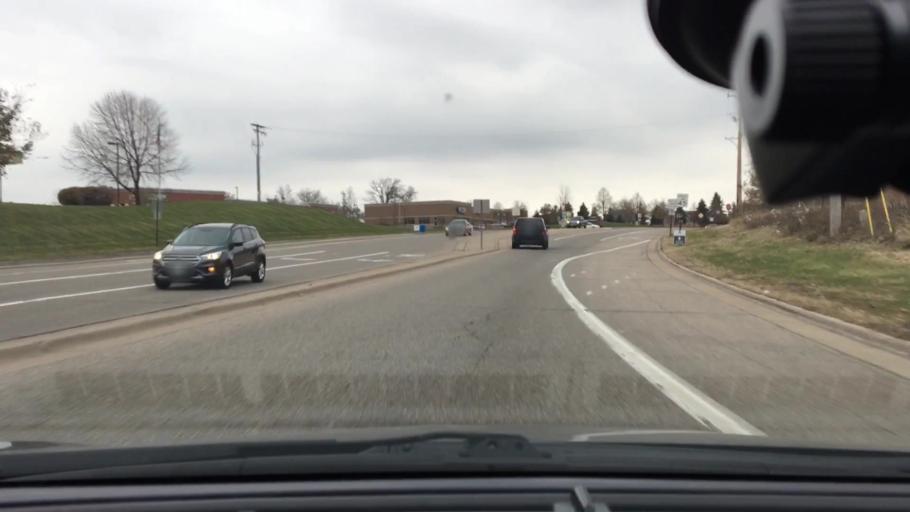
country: US
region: Minnesota
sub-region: Hennepin County
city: Corcoran
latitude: 45.0441
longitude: -93.5258
